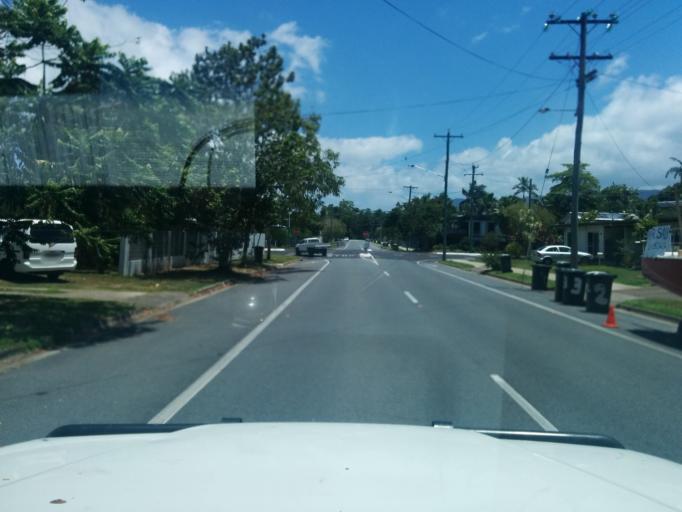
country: AU
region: Queensland
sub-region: Cairns
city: Cairns
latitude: -16.9026
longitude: 145.7442
